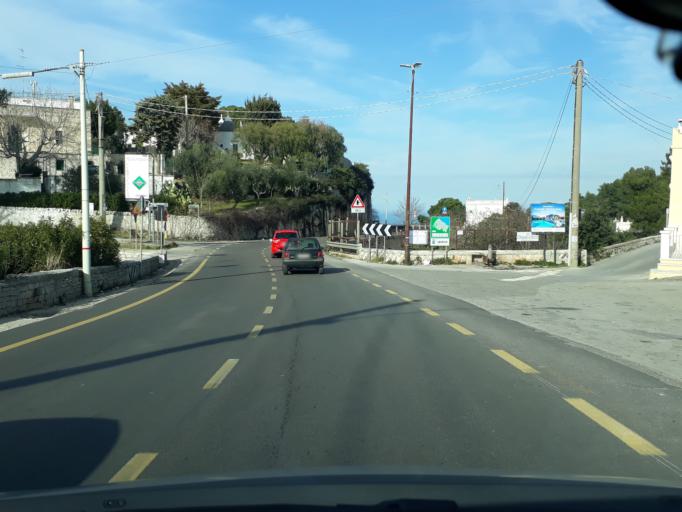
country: IT
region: Apulia
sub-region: Provincia di Brindisi
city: Lamie di Olimpie-Selva
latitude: 40.8004
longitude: 17.3523
